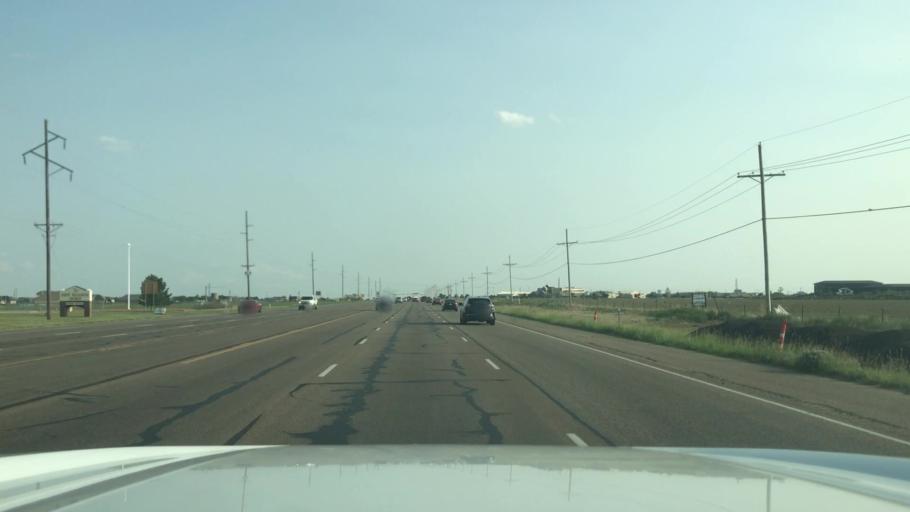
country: US
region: Texas
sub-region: Potter County
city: Amarillo
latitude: 35.1558
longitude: -101.9383
